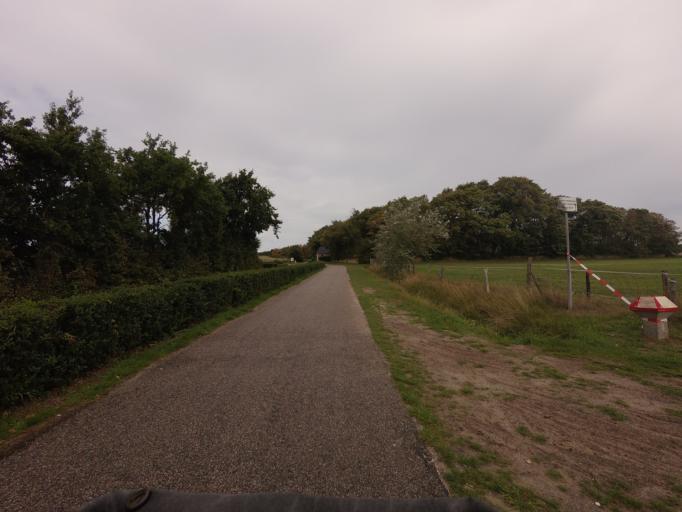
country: NL
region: Friesland
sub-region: Gemeente Ameland
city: Nes
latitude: 53.4475
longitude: 5.7818
